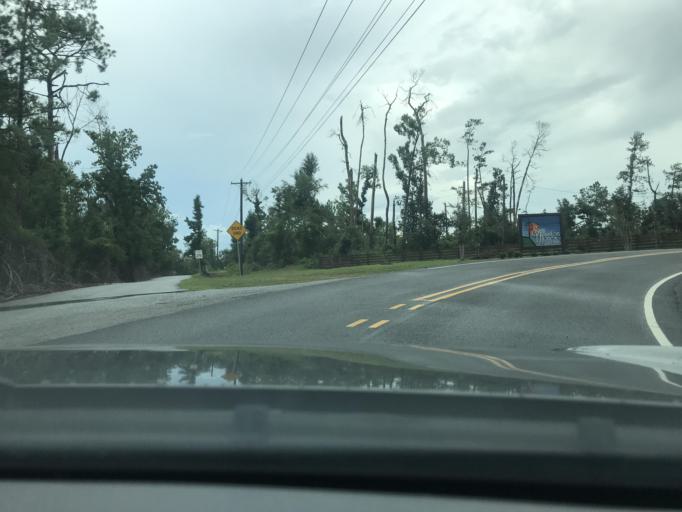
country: US
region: Louisiana
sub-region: Calcasieu Parish
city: Westlake
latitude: 30.3008
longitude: -93.2559
